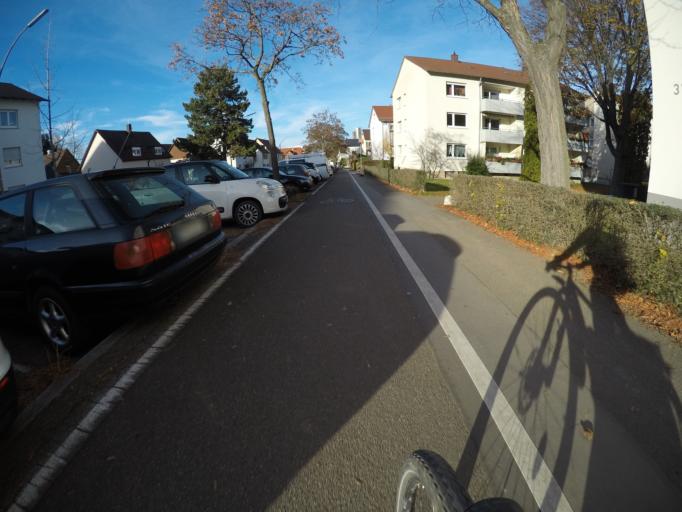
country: DE
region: Baden-Wuerttemberg
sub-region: Regierungsbezirk Stuttgart
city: Fellbach
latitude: 48.8072
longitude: 9.2831
